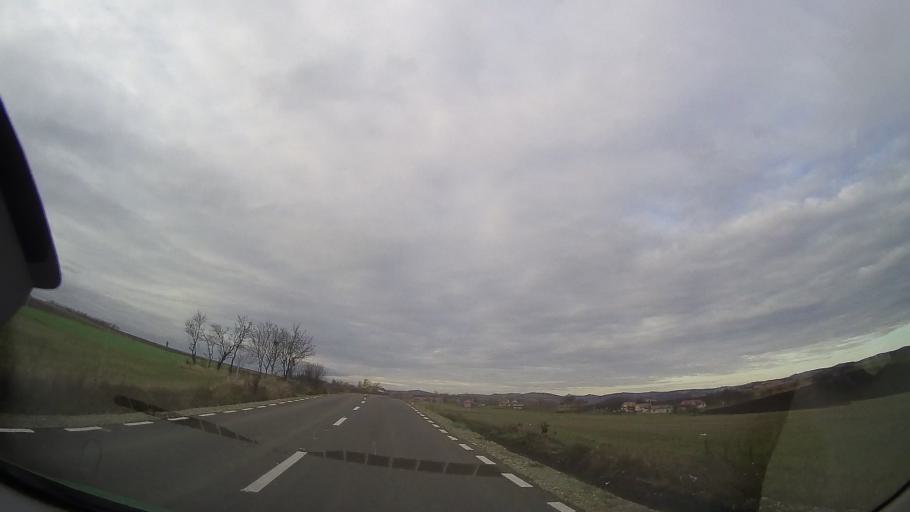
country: RO
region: Bistrita-Nasaud
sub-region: Comuna Teaca
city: Ocnita
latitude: 46.8277
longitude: 24.4725
